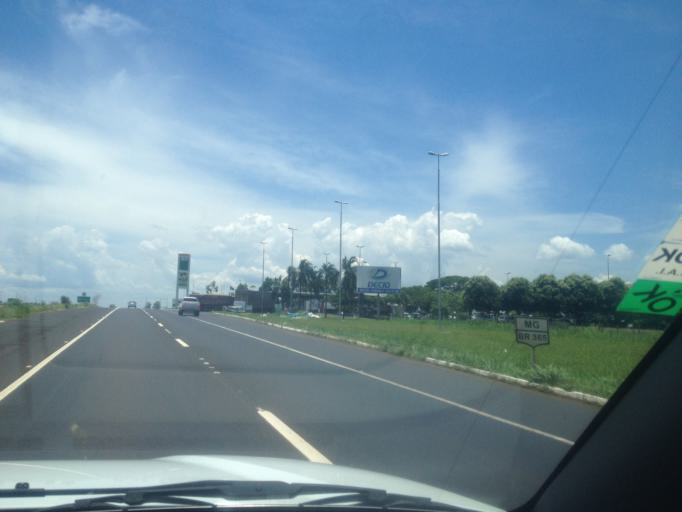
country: BR
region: Minas Gerais
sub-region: Uberlandia
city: Uberlandia
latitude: -18.8922
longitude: -48.4209
